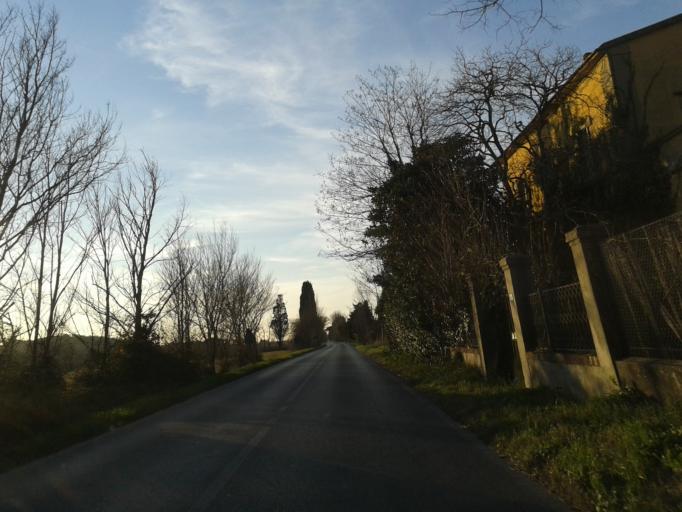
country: IT
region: Tuscany
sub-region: Provincia di Livorno
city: Guasticce
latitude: 43.5973
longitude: 10.4313
